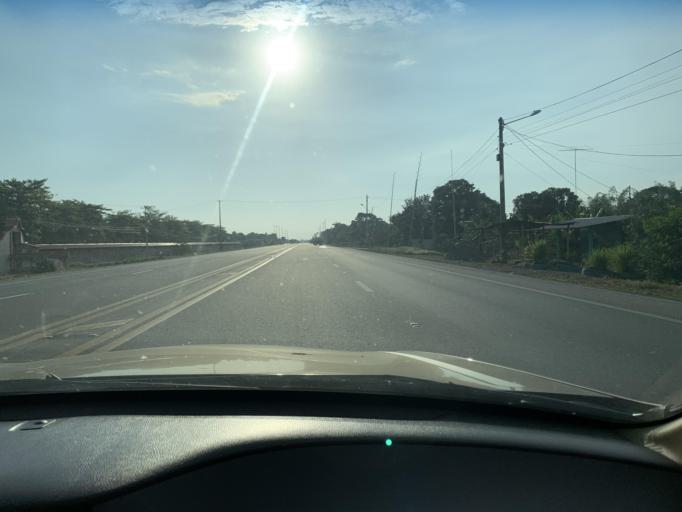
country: EC
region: Guayas
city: Naranjito
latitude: -2.2560
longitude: -79.5981
